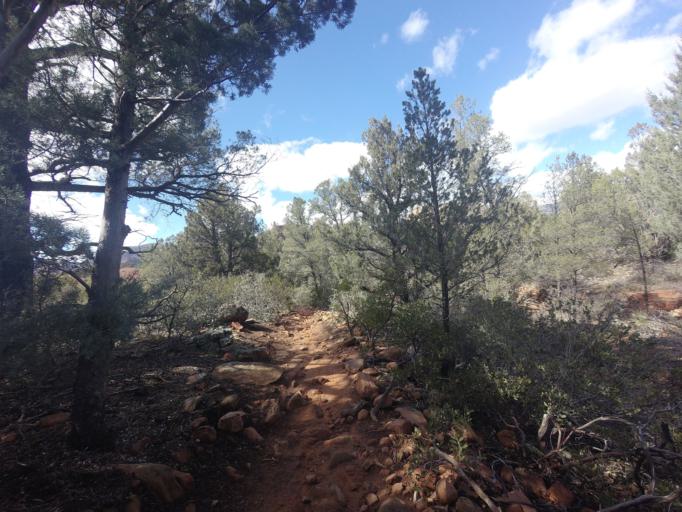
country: US
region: Arizona
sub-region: Yavapai County
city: West Sedona
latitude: 34.9004
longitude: -111.8246
